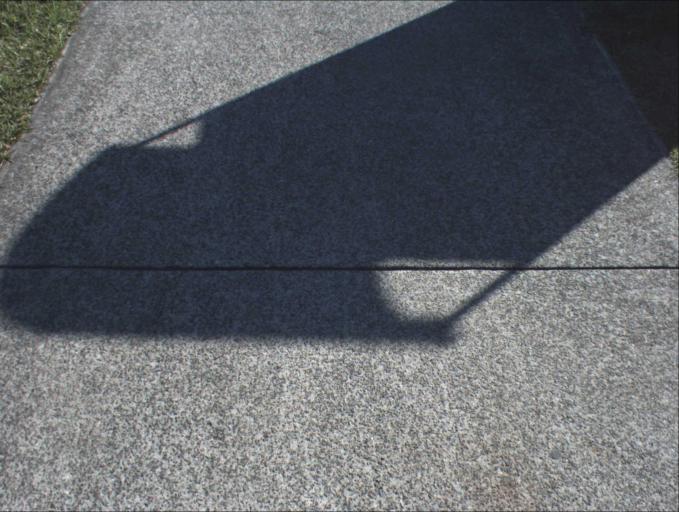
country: AU
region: Queensland
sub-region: Logan
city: Logan City
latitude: -27.6411
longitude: 153.1296
